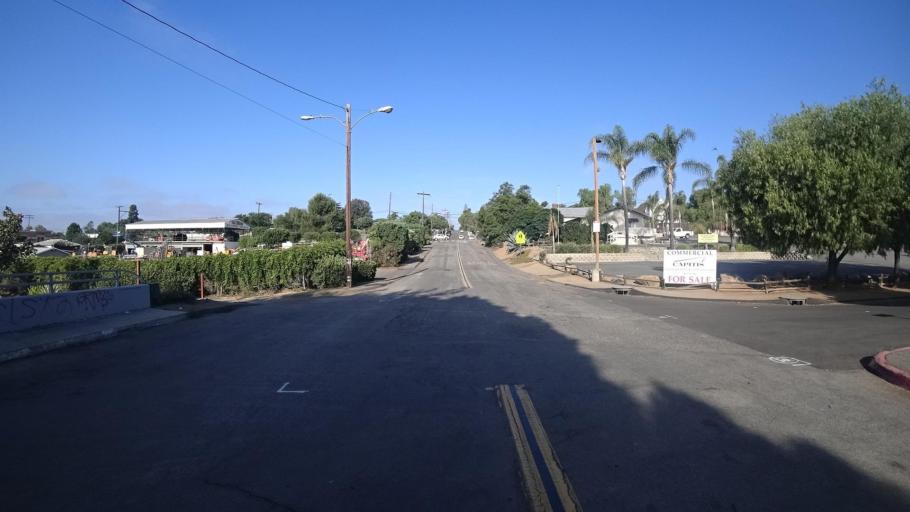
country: US
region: California
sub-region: San Diego County
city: Fallbrook
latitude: 33.3803
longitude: -117.2524
